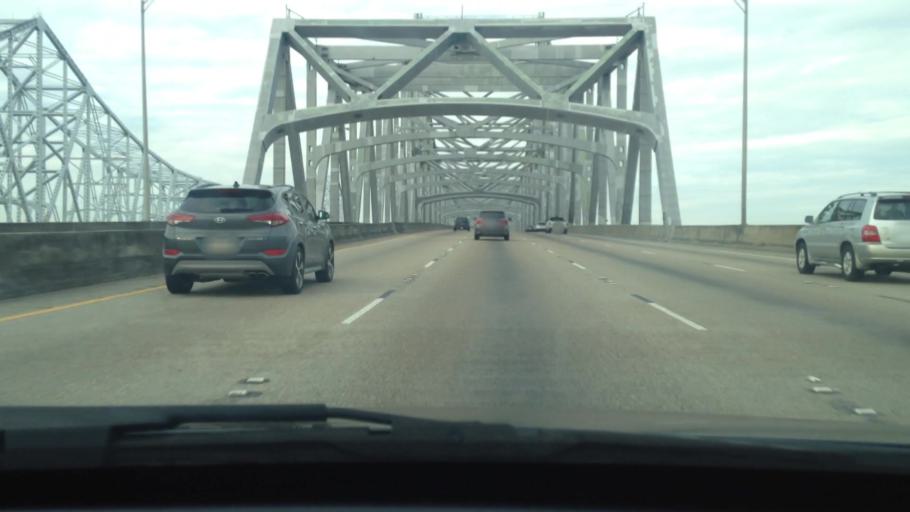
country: US
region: Louisiana
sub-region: Jefferson Parish
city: Gretna
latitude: 29.9388
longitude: -90.0516
